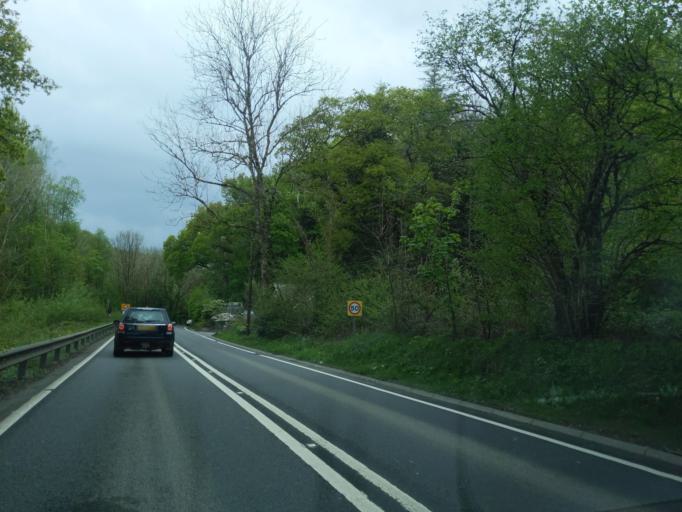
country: GB
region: England
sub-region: Cornwall
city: Lostwithiel
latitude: 50.4548
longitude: -4.5760
